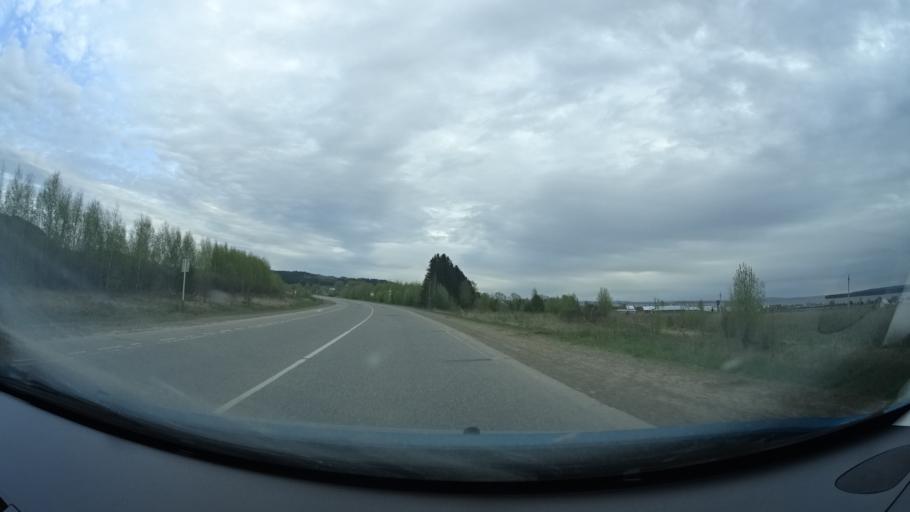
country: RU
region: Perm
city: Osa
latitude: 57.3355
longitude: 55.5843
